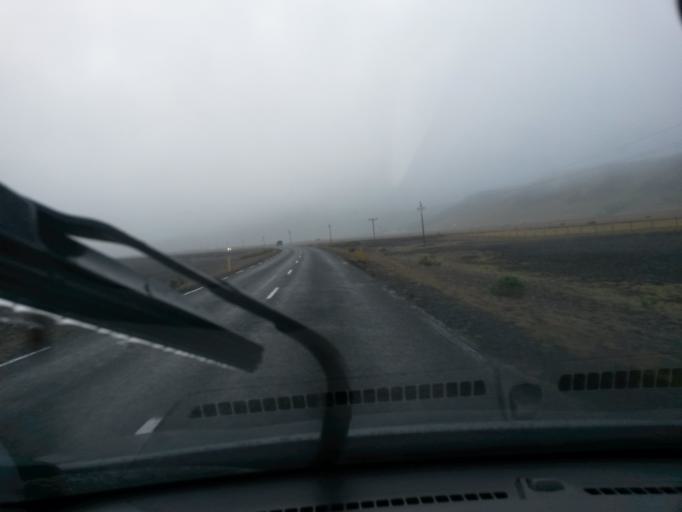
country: IS
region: South
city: Vestmannaeyjar
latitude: 63.5146
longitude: -19.4606
